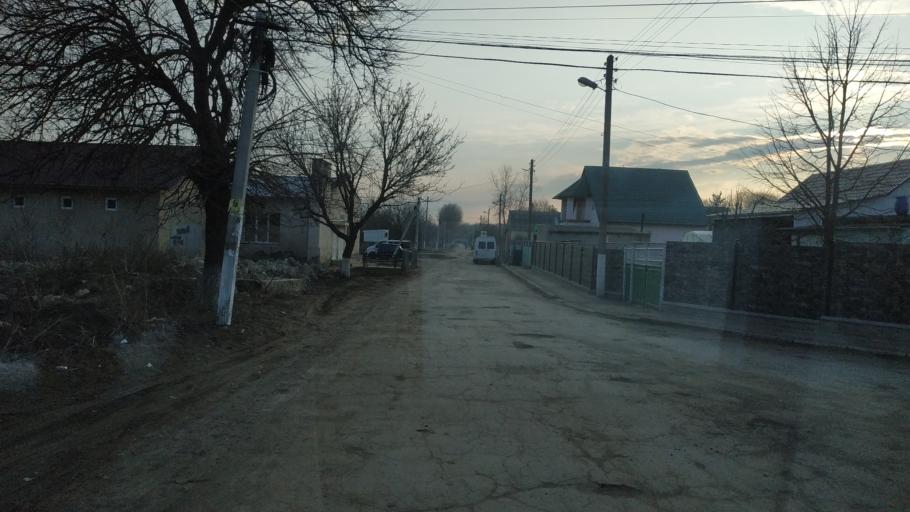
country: MD
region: Hincesti
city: Dancu
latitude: 46.7144
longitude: 28.3490
